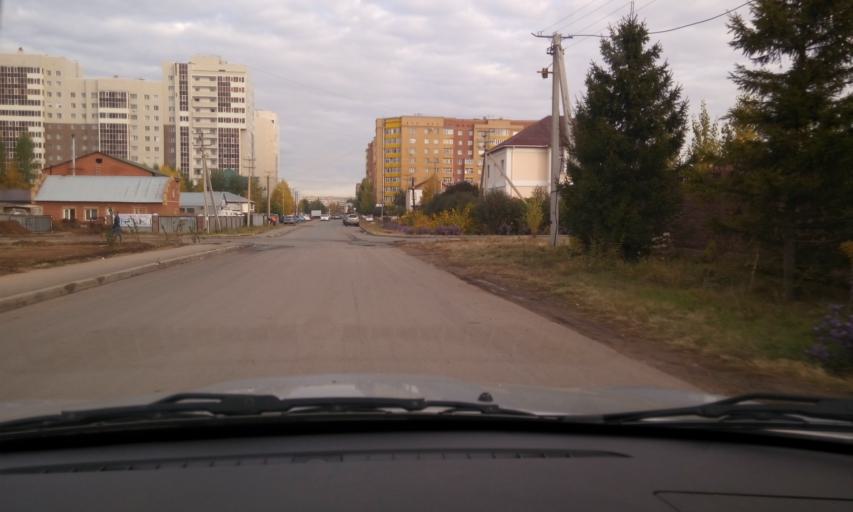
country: KZ
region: Astana Qalasy
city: Astana
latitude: 51.1388
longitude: 71.4868
